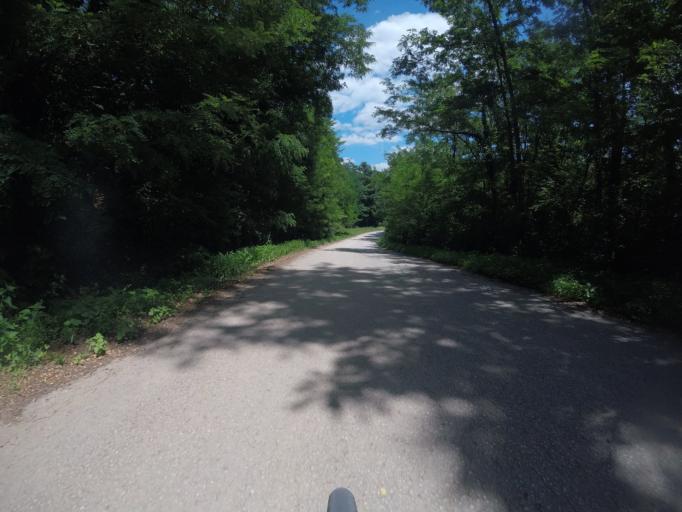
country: HR
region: Karlovacka
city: Ozalj
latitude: 45.6713
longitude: 15.4178
